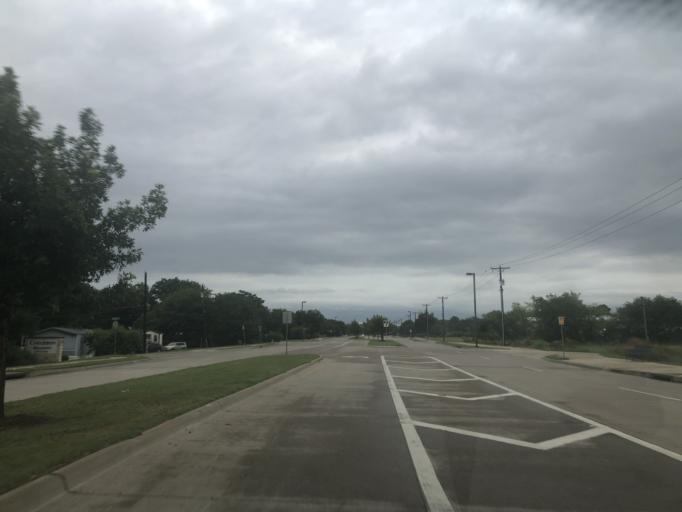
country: US
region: Texas
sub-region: Dallas County
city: Irving
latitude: 32.7829
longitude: -96.9700
